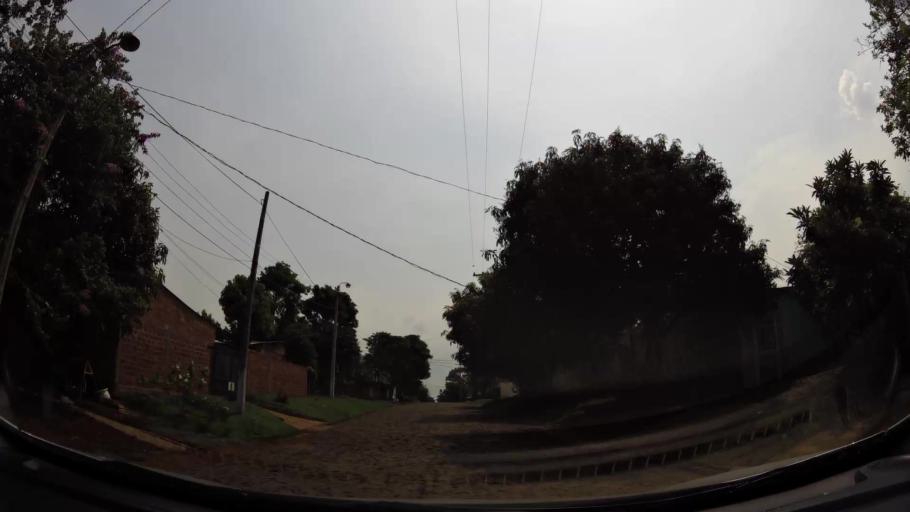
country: PY
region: Alto Parana
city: Presidente Franco
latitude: -25.5446
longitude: -54.6247
